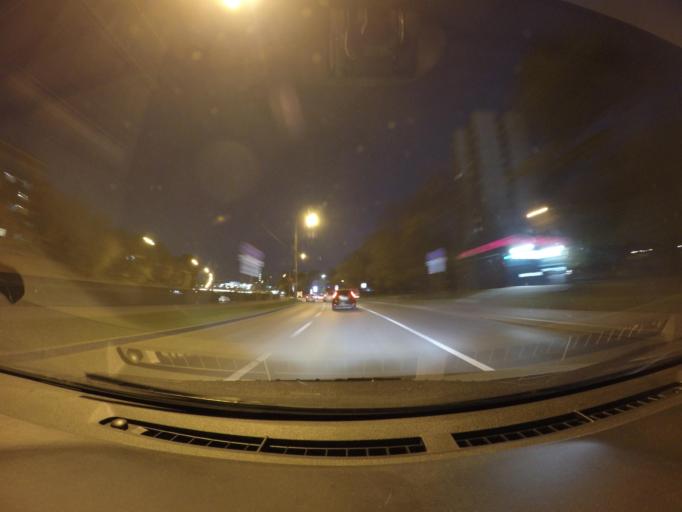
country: RU
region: Moskovskaya
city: Bogorodskoye
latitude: 55.8002
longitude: 37.6983
